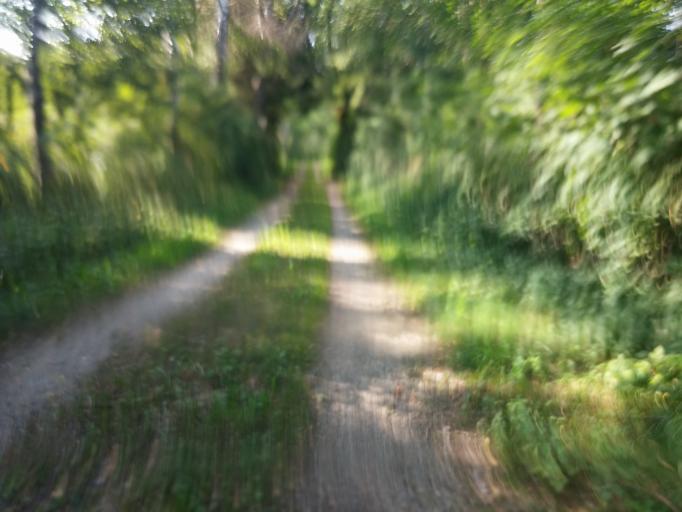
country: DE
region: Baden-Wuerttemberg
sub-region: Tuebingen Region
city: Aitrach
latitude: 47.9471
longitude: 10.0913
